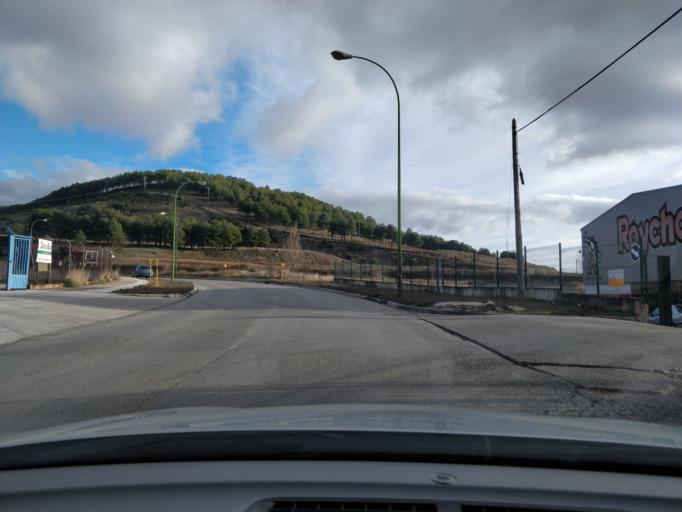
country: ES
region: Castille and Leon
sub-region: Provincia de Burgos
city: Villalbilla de Burgos
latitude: 42.3635
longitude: -3.7516
